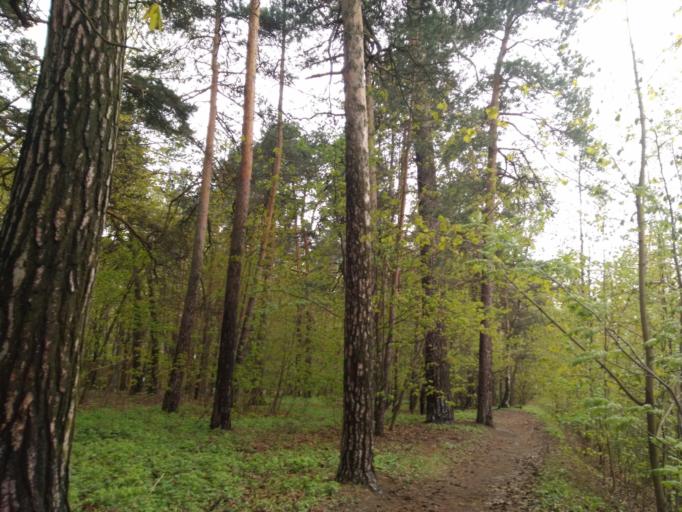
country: RU
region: Moscow
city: Shchukino
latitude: 55.7873
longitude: 37.4391
